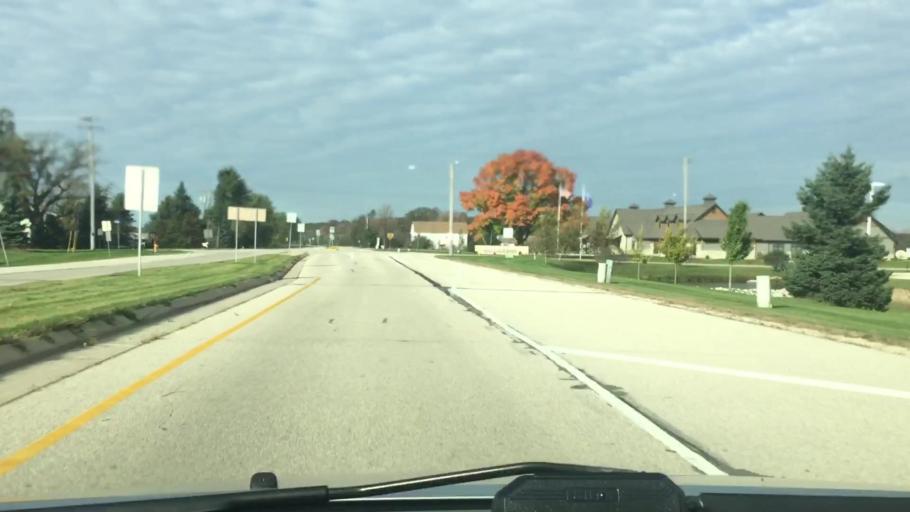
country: US
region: Wisconsin
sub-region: Waukesha County
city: Dousman
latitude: 43.0623
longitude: -88.4802
